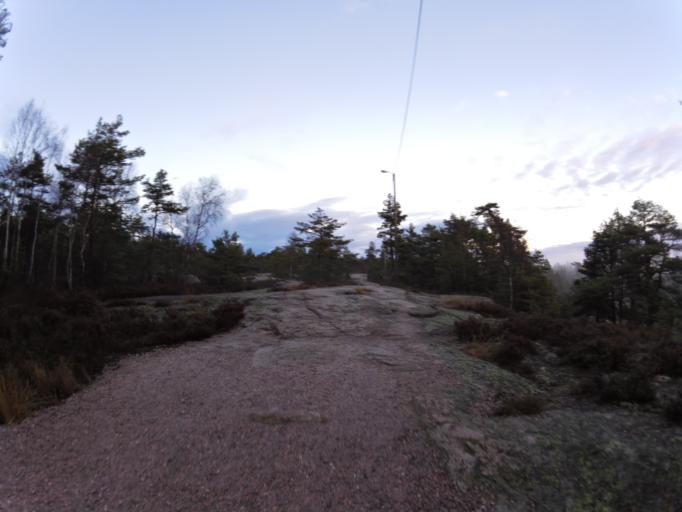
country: NO
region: Ostfold
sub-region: Fredrikstad
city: Fredrikstad
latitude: 59.2644
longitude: 10.9736
